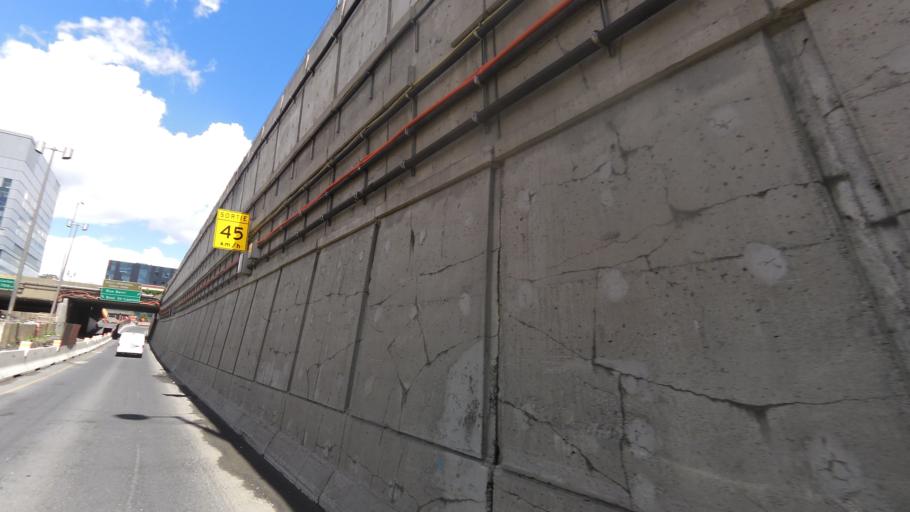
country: CA
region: Quebec
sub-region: Montreal
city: Montreal
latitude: 45.5082
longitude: -73.5571
